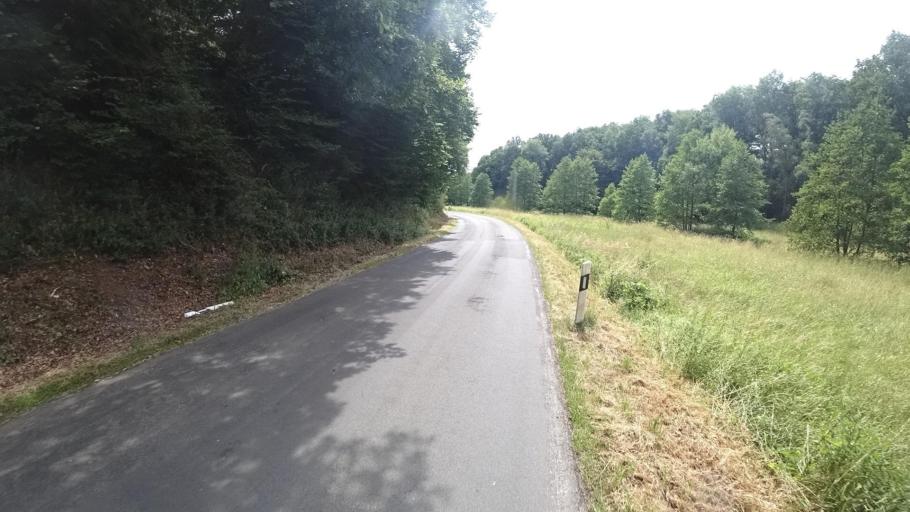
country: DE
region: Rheinland-Pfalz
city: Walterschen
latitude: 50.6803
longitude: 7.5745
